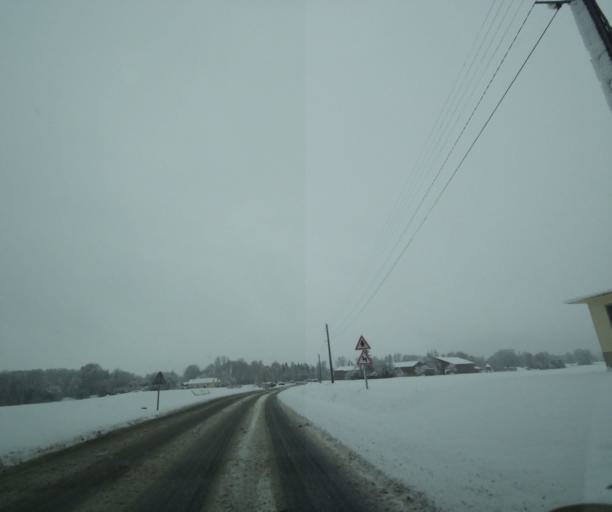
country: FR
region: Champagne-Ardenne
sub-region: Departement de la Haute-Marne
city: Saint-Dizier
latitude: 48.5883
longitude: 4.9018
